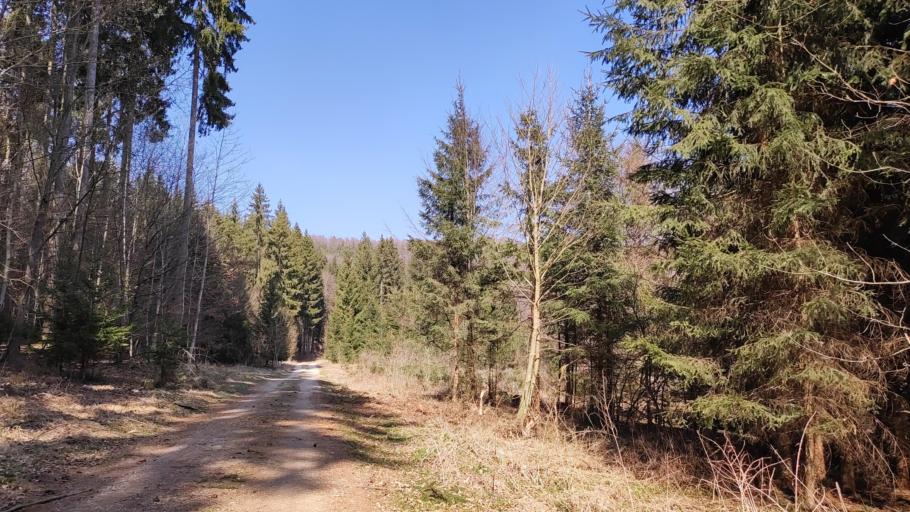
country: DE
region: Baden-Wuerttemberg
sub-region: Tuebingen Region
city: Borslingen
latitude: 48.5248
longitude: 10.0488
